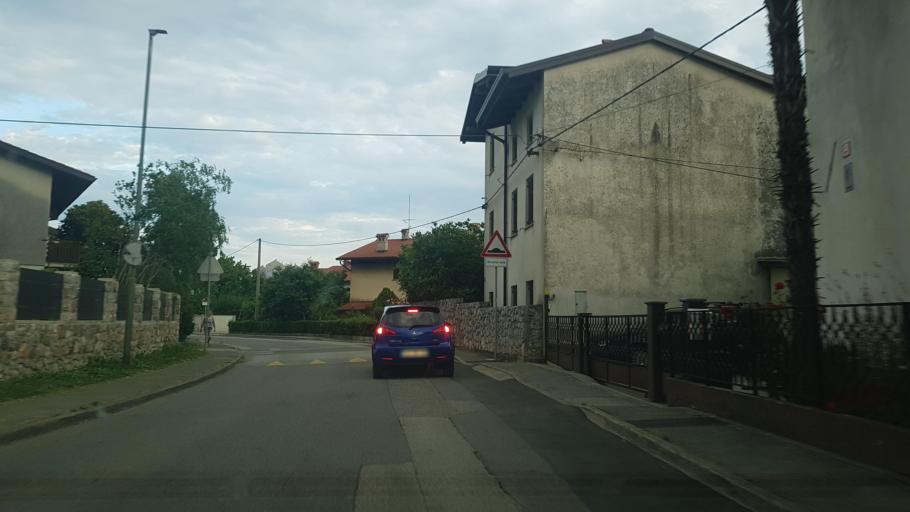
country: SI
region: Nova Gorica
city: Solkan
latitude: 45.9681
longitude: 13.6493
